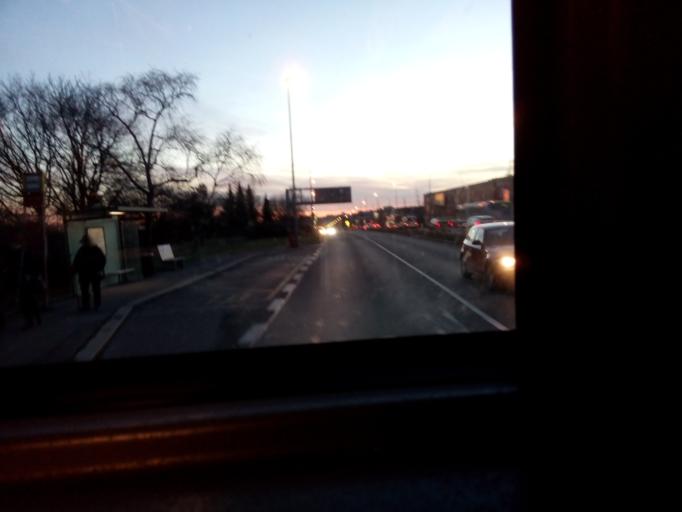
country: CZ
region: Central Bohemia
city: Hostivice
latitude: 50.0935
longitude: 14.3045
